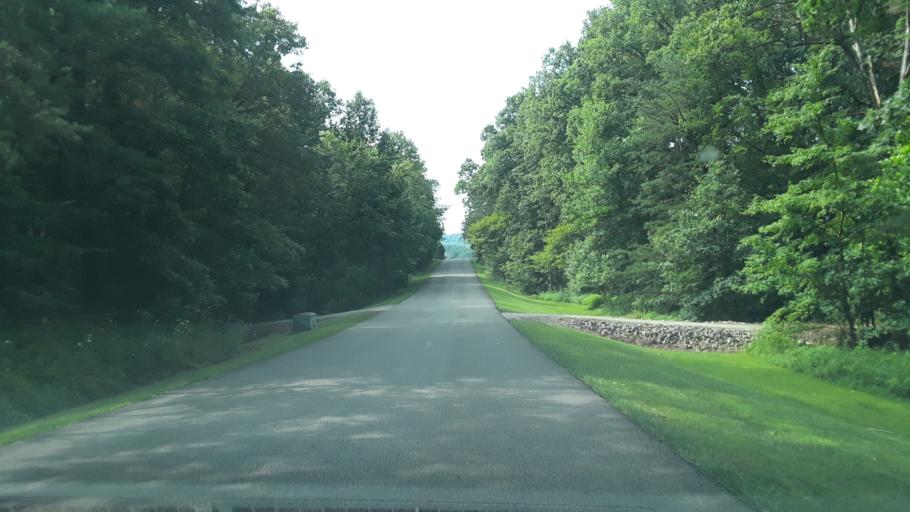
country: US
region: Indiana
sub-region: Clark County
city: Sellersburg
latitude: 38.4604
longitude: -85.8654
